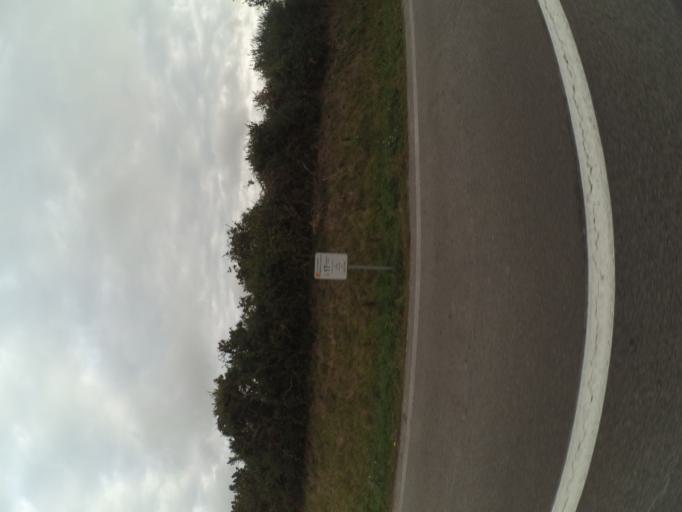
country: FR
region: Brittany
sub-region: Departement du Morbihan
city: Theix
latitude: 47.6343
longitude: -2.6604
